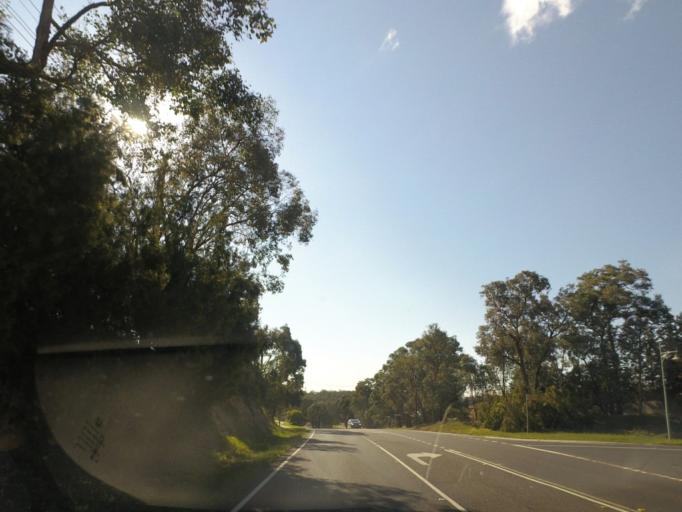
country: AU
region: Victoria
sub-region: Manningham
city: Donvale
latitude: -37.7710
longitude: 145.1837
